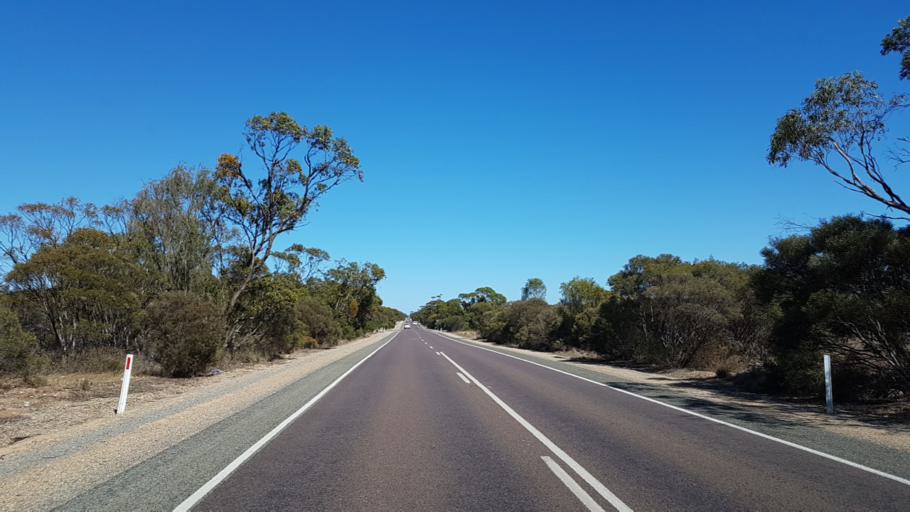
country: AU
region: South Australia
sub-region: Copper Coast
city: Kadina
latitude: -34.0508
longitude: 137.9812
